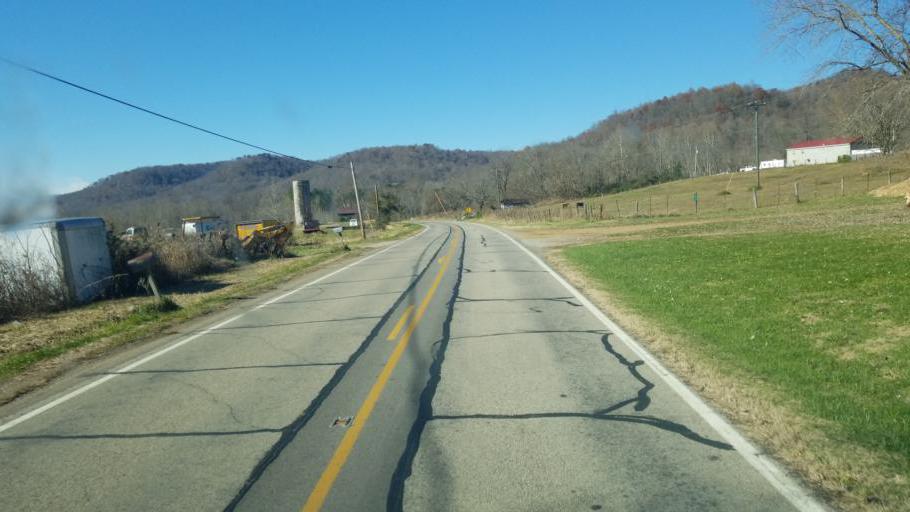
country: US
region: Kentucky
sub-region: Lewis County
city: Vanceburg
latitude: 38.6364
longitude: -83.2201
